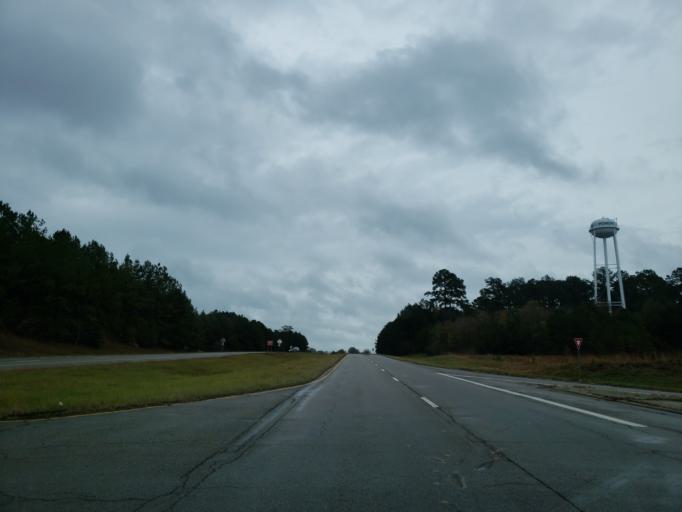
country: US
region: Mississippi
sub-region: Jones County
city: Laurel
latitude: 31.6978
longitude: -89.1019
